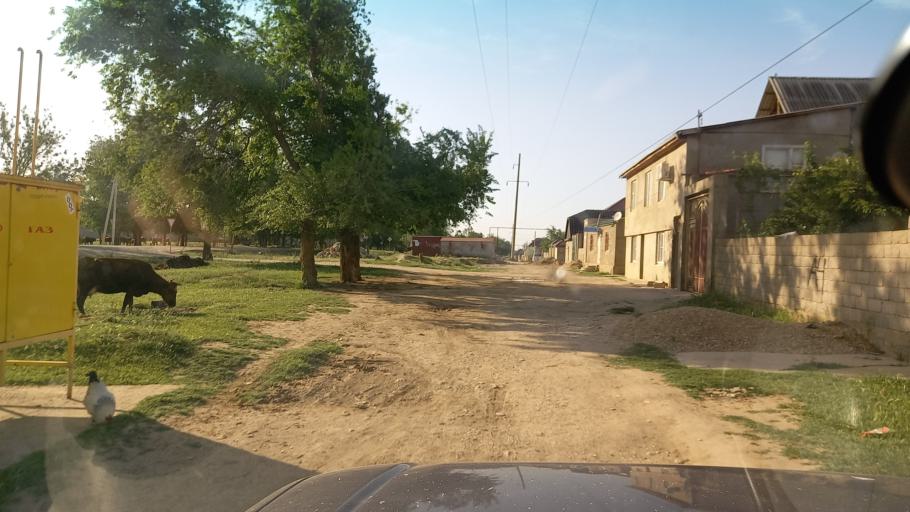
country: RU
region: Dagestan
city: Shamkhal-Termen
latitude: 43.0106
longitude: 47.3311
